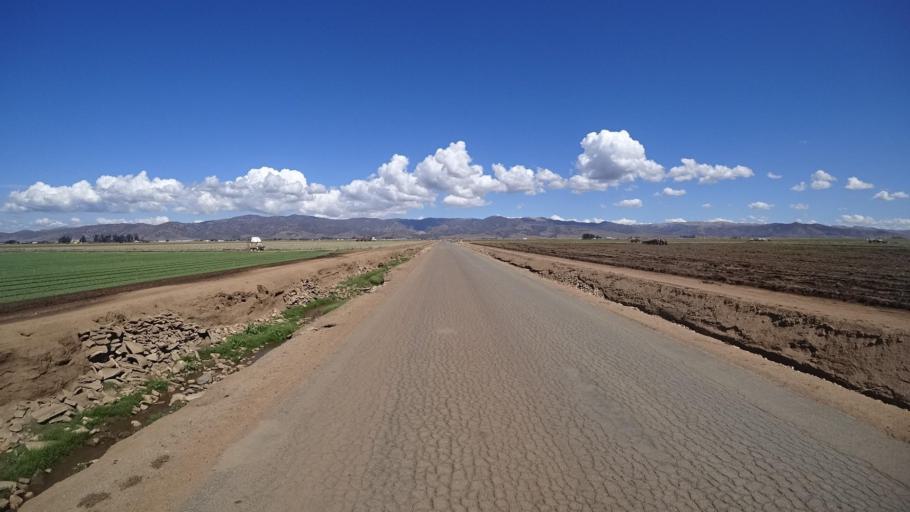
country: US
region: California
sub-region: Monterey County
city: Chualar
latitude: 36.5958
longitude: -121.5250
